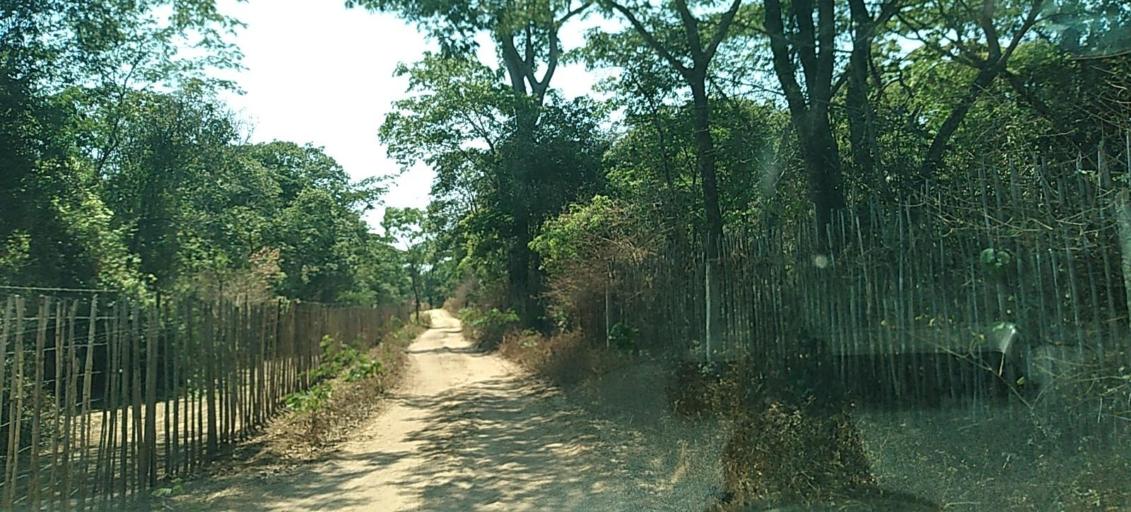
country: ZM
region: Copperbelt
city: Luanshya
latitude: -13.0092
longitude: 28.4611
